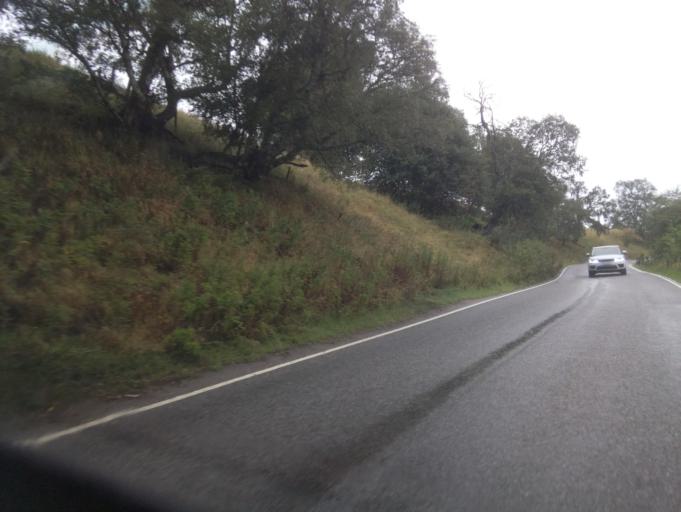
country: GB
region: Scotland
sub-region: Highland
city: Grantown on Spey
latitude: 57.2571
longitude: -3.4066
